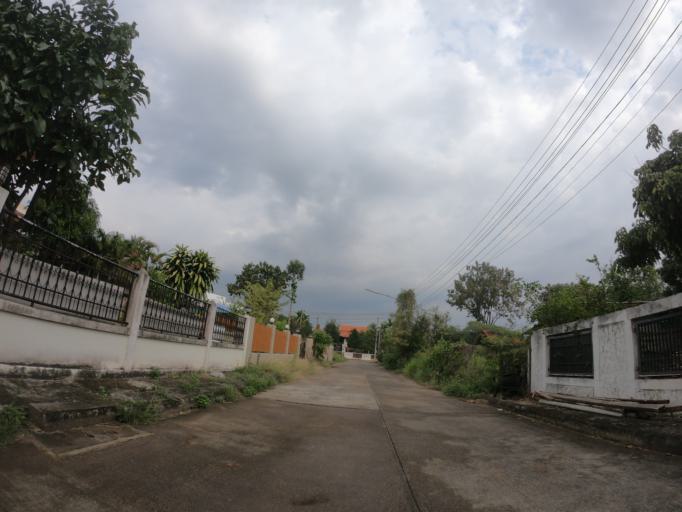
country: TH
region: Chiang Mai
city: Chiang Mai
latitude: 18.7605
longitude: 98.9736
